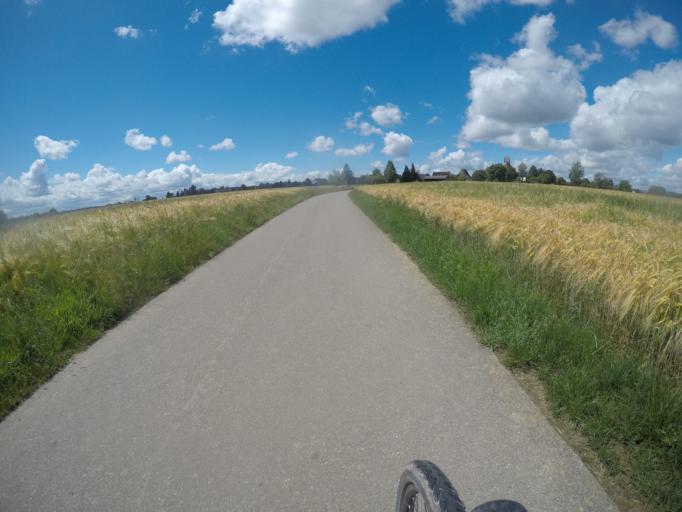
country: DE
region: Baden-Wuerttemberg
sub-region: Karlsruhe Region
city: Horb am Neckar
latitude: 48.4687
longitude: 8.7206
